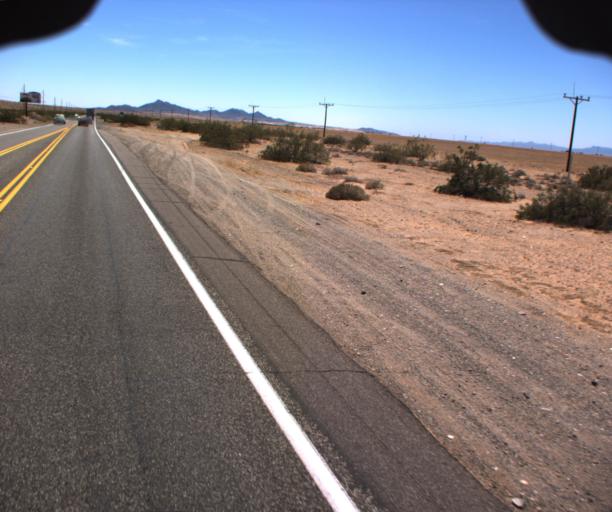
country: US
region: Arizona
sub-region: La Paz County
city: Parker
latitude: 34.1272
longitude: -114.2795
